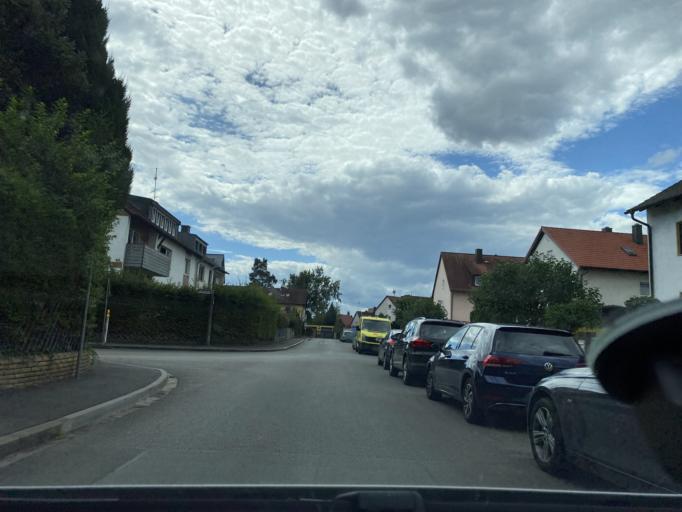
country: DE
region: Bavaria
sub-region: Regierungsbezirk Mittelfranken
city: Furth
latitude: 49.5091
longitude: 10.9818
